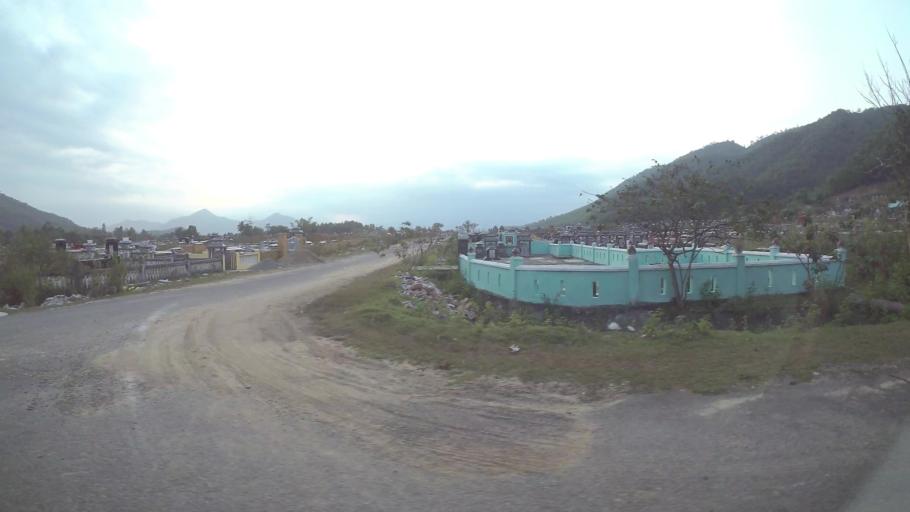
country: VN
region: Da Nang
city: Lien Chieu
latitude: 16.0608
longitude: 108.1245
